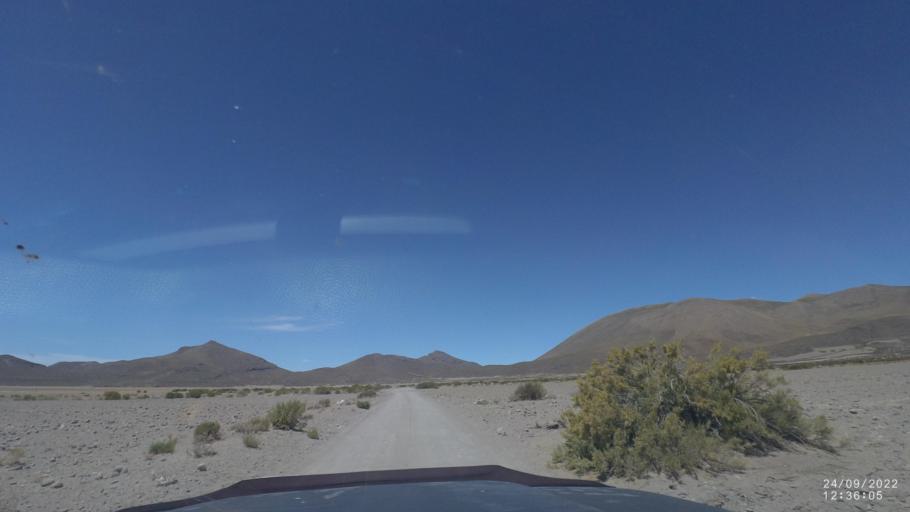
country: BO
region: Potosi
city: Colchani
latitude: -19.7850
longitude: -67.5901
